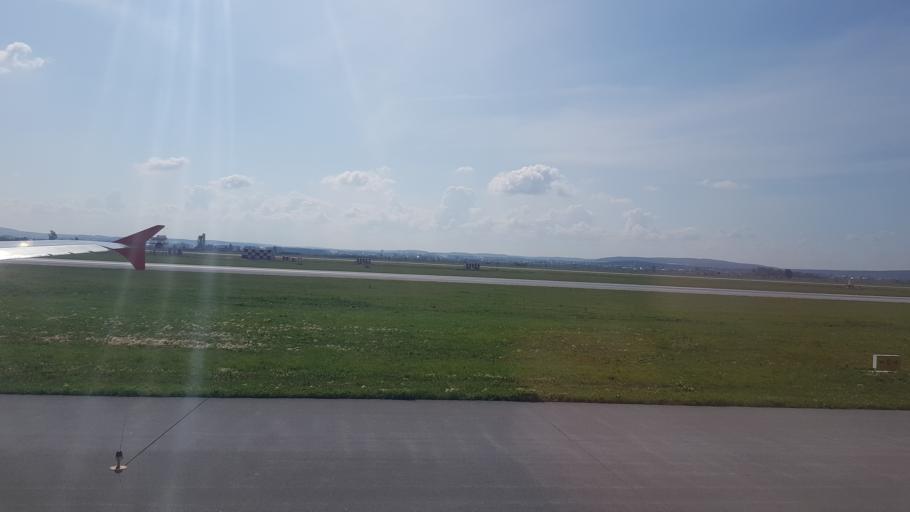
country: RU
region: Sverdlovsk
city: Istok
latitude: 56.7463
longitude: 60.8015
